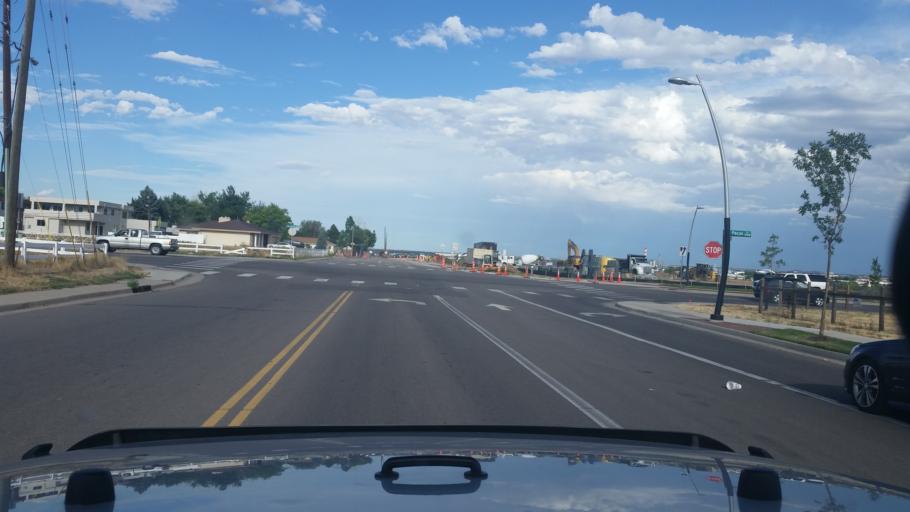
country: US
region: Colorado
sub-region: Adams County
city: Twin Lakes
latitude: 39.8200
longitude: -105.0068
